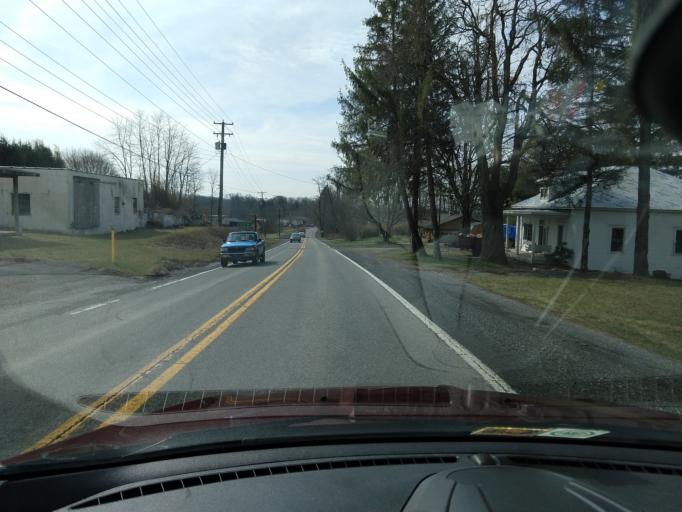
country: US
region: West Virginia
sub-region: Greenbrier County
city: Lewisburg
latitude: 37.8642
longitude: -80.4101
